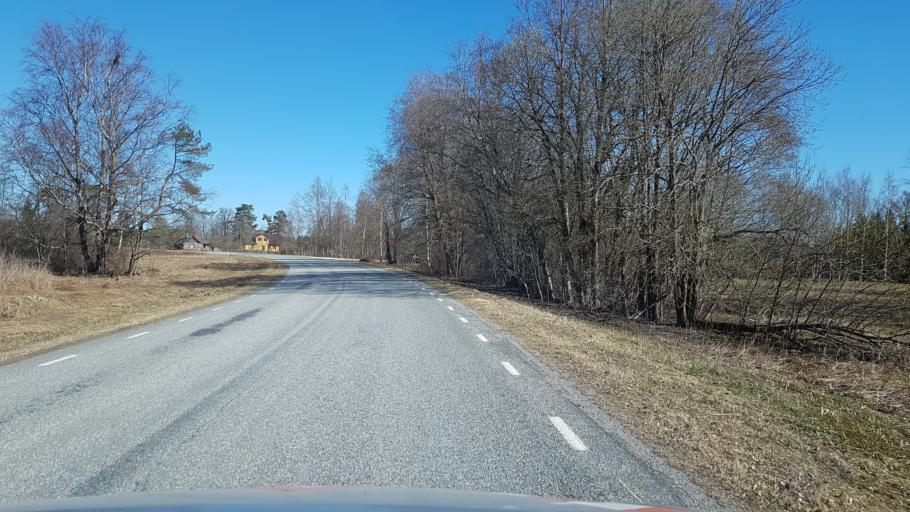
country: EE
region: Laeaene-Virumaa
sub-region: Haljala vald
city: Haljala
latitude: 59.4643
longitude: 26.2408
